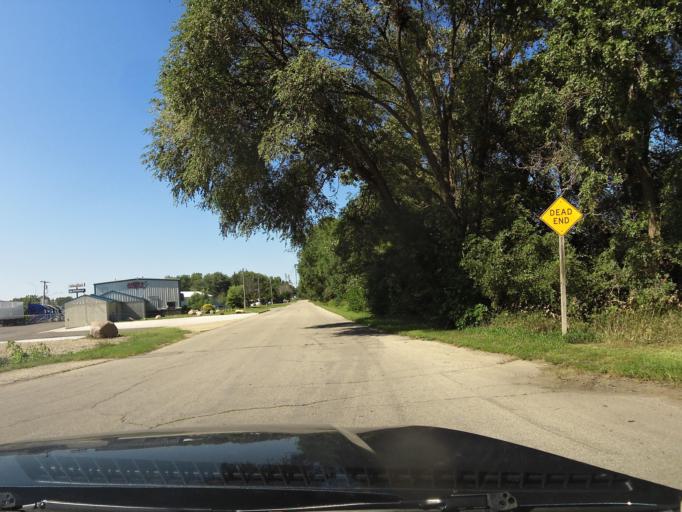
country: US
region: Iowa
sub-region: Black Hawk County
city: Waterloo
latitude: 42.4694
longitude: -92.3171
